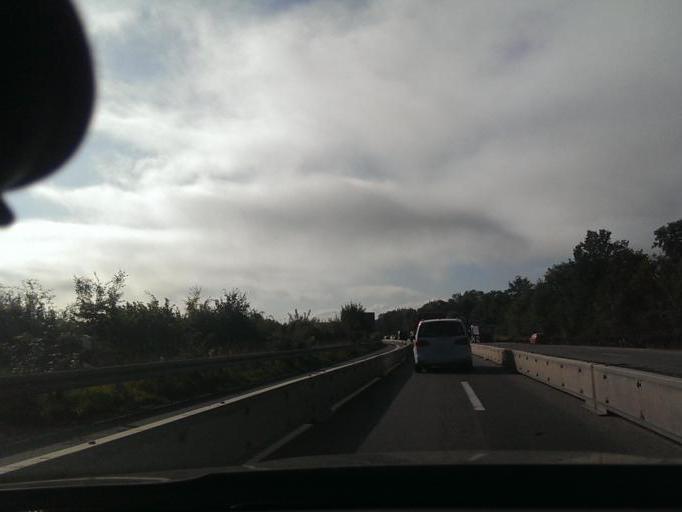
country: DE
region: Lower Saxony
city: Vienenburg
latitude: 51.9795
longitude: 10.5581
